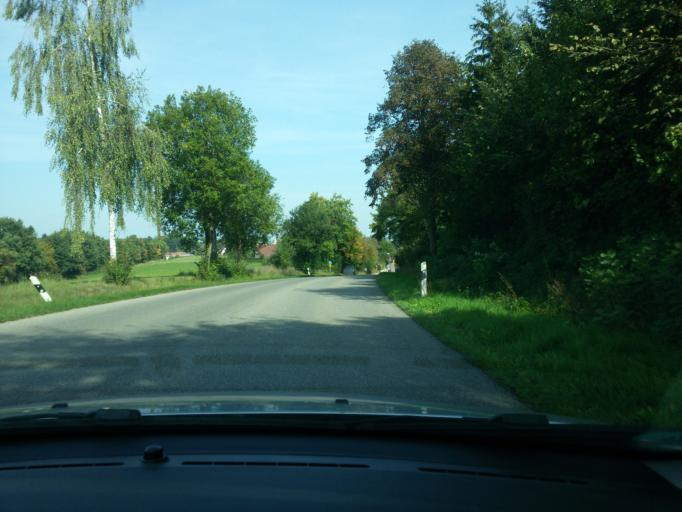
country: DE
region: Bavaria
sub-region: Swabia
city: Ziemetshausen
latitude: 48.2892
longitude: 10.5198
